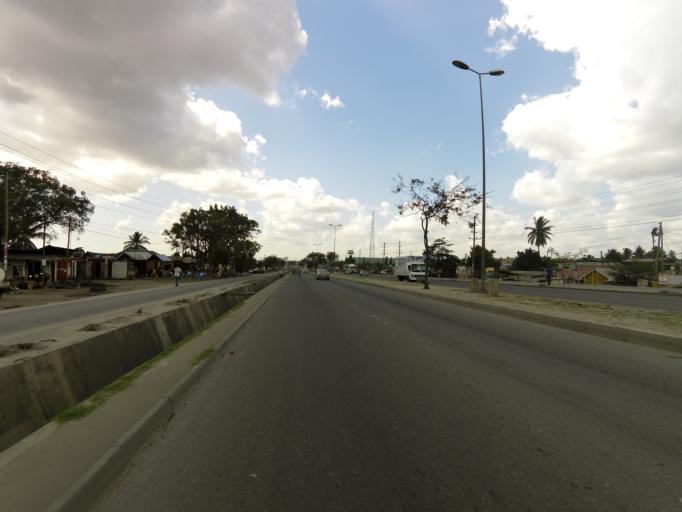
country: TZ
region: Dar es Salaam
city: Magomeni
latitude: -6.8145
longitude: 39.2191
